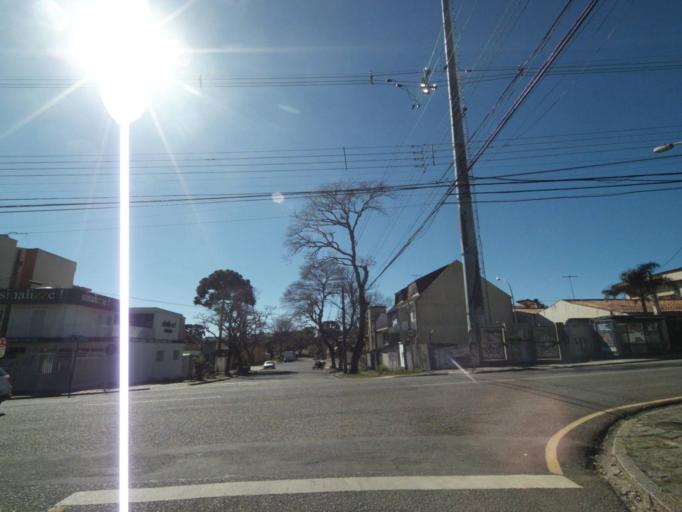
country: BR
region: Parana
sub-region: Curitiba
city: Curitiba
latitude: -25.4233
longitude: -49.2443
